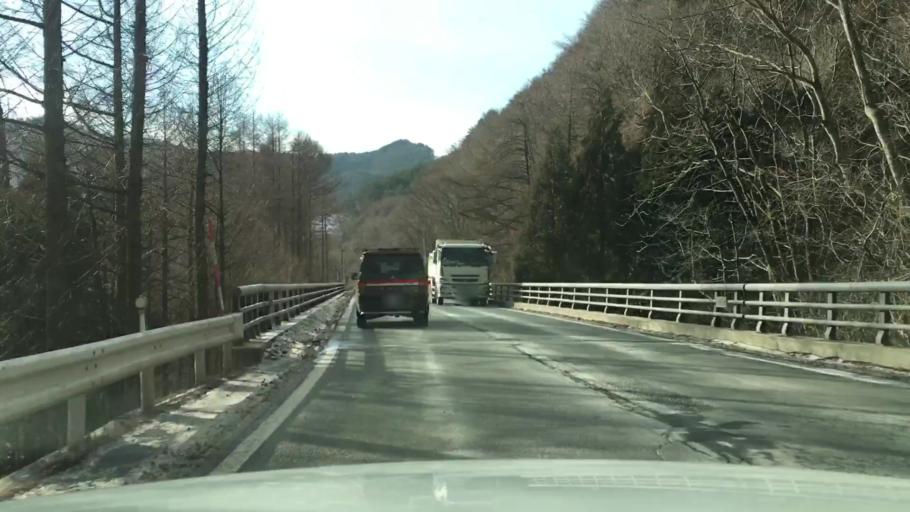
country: JP
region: Iwate
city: Morioka-shi
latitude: 39.6661
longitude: 141.3116
